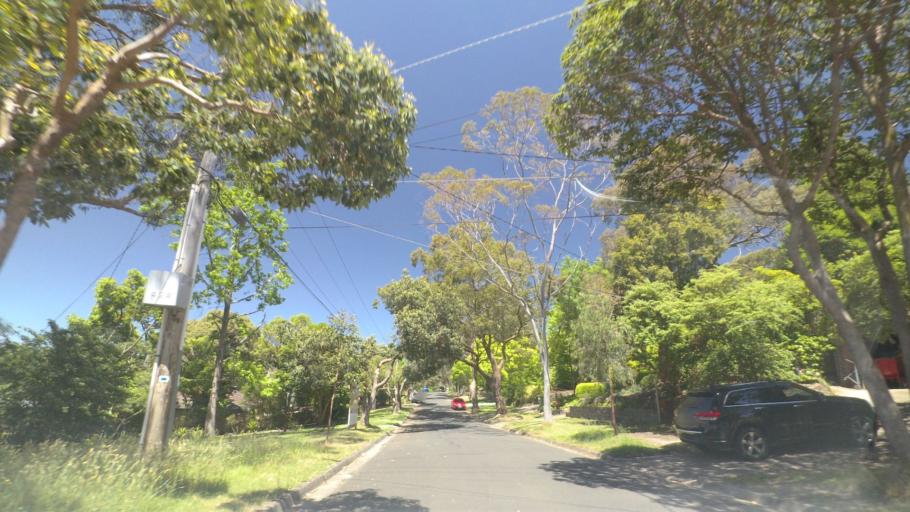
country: AU
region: Victoria
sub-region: Maroondah
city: Croydon North
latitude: -37.7727
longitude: 145.2854
